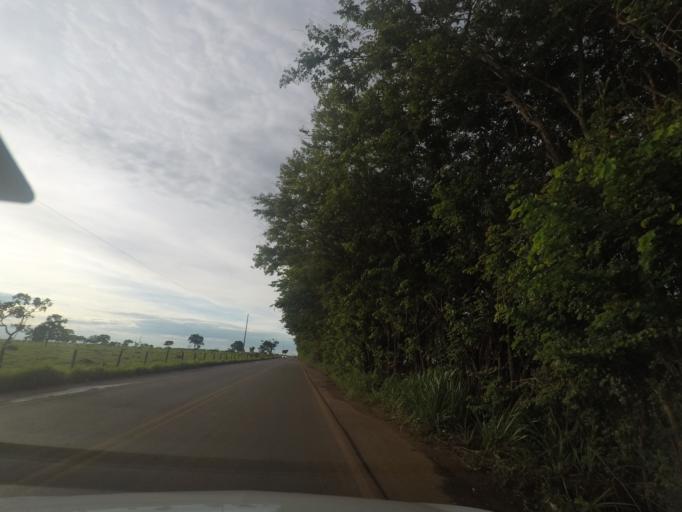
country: BR
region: Goias
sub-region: Trindade
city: Trindade
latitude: -16.7236
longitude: -49.4277
